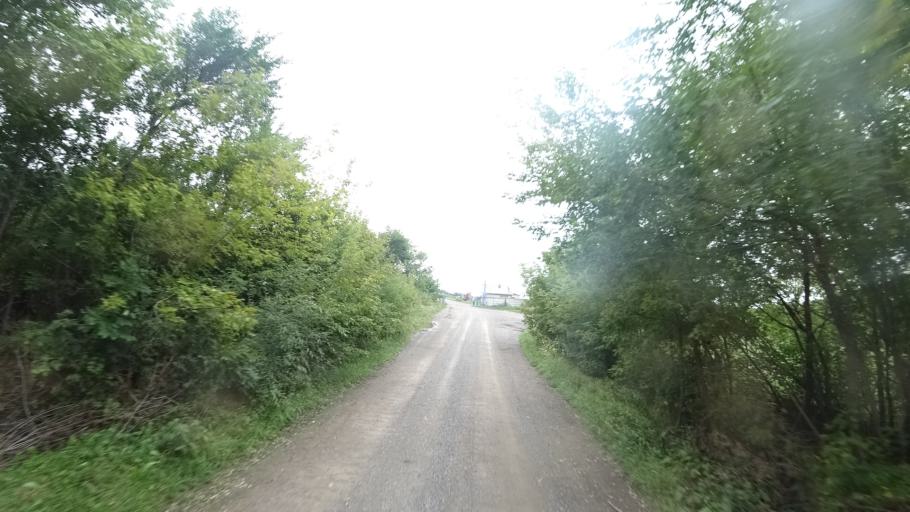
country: RU
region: Primorskiy
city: Monastyrishche
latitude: 44.2673
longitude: 132.4589
